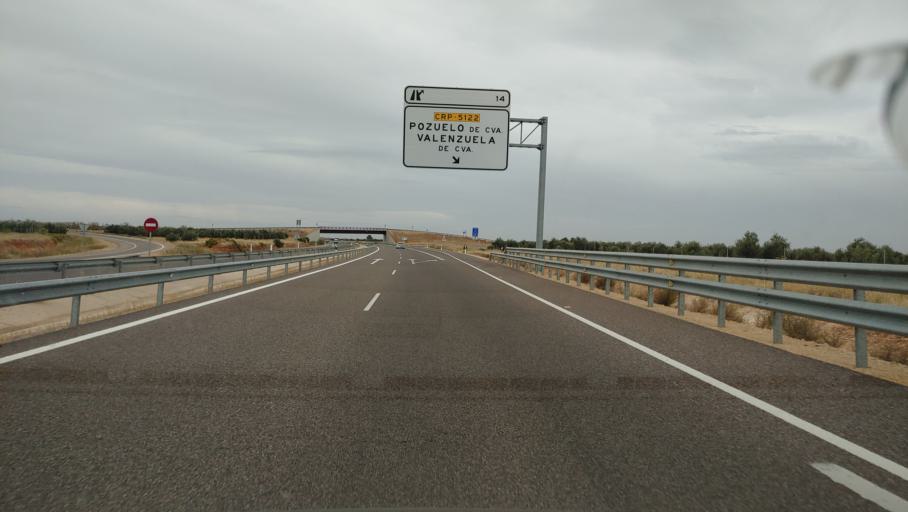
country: ES
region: Castille-La Mancha
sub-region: Provincia de Ciudad Real
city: Valenzuela de Calatrava
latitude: 38.9023
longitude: -3.8102
